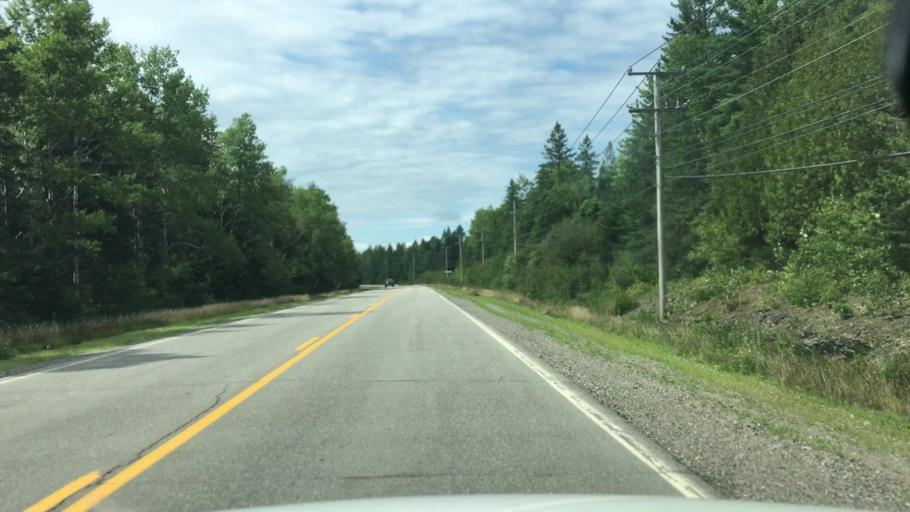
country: CA
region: New Brunswick
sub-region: Charlotte County
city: Saint Andrews
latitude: 44.9551
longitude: -67.1294
